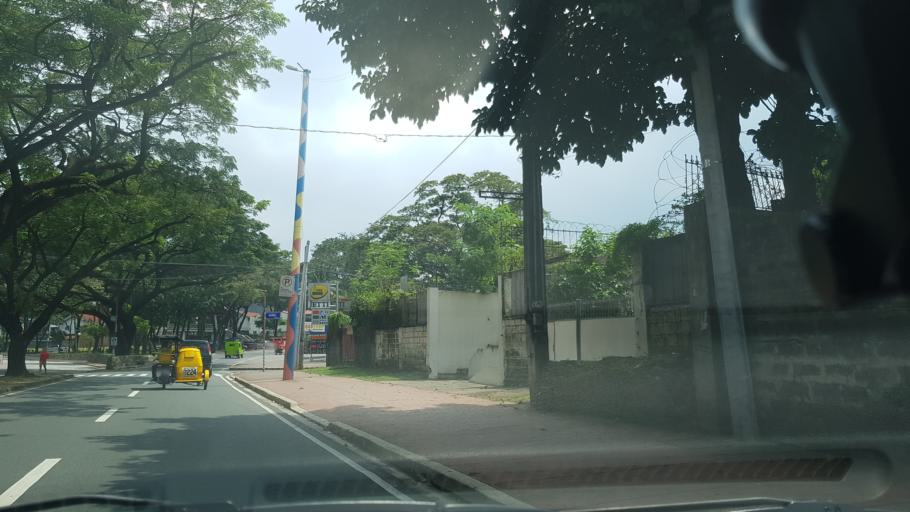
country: PH
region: Calabarzon
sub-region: Province of Rizal
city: Antipolo
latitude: 14.6503
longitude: 121.1132
